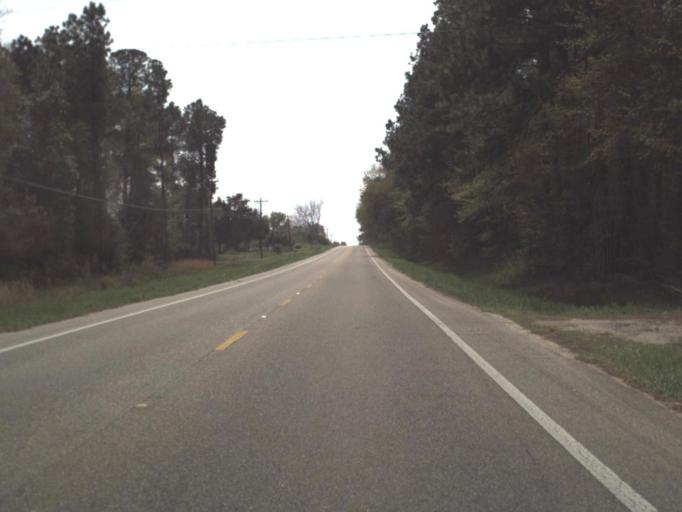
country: US
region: Florida
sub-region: Jackson County
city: Graceville
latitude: 30.9012
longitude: -85.5227
